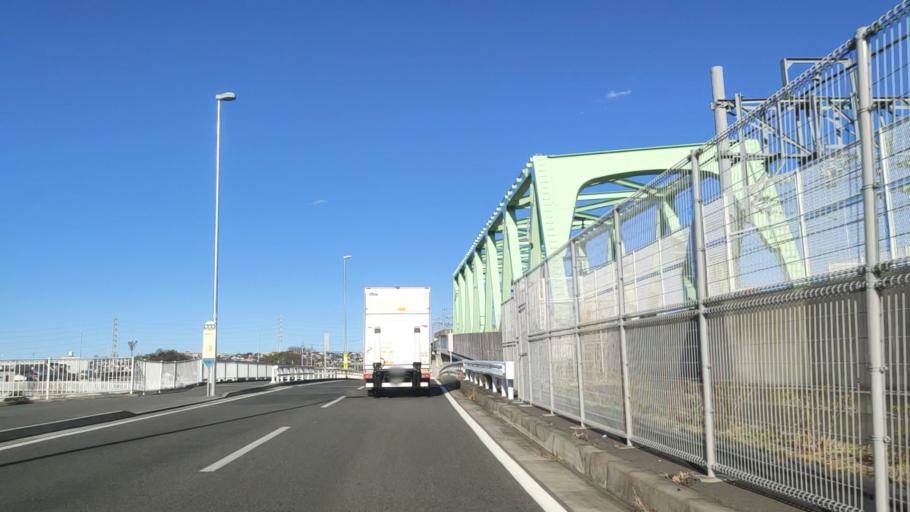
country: JP
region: Tokyo
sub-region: Machida-shi
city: Machida
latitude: 35.5260
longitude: 139.5466
